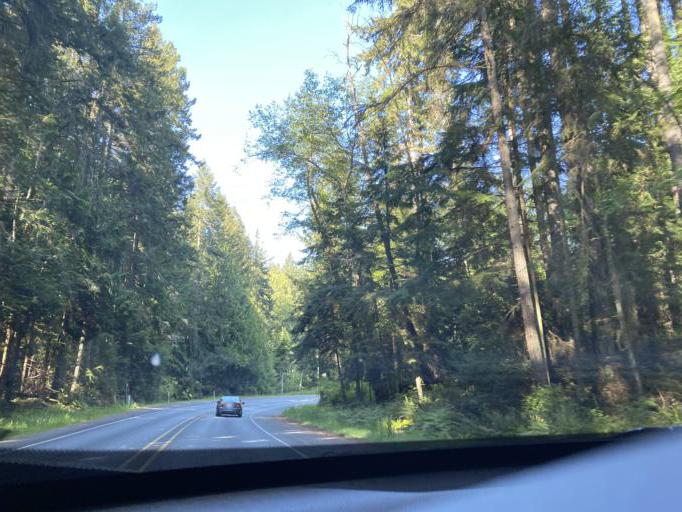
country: US
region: Washington
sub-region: Island County
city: Langley
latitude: 48.0327
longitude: -122.4311
